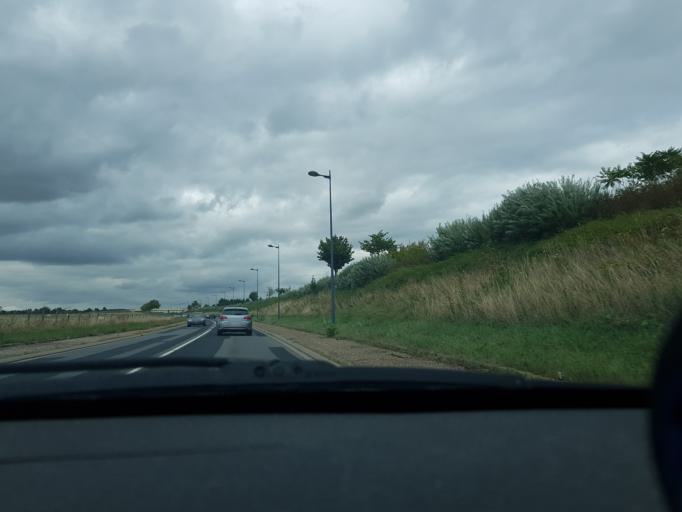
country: FR
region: Lorraine
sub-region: Departement de Meurthe-et-Moselle
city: Saulxures-les-Nancy
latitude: 48.6894
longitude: 6.2366
